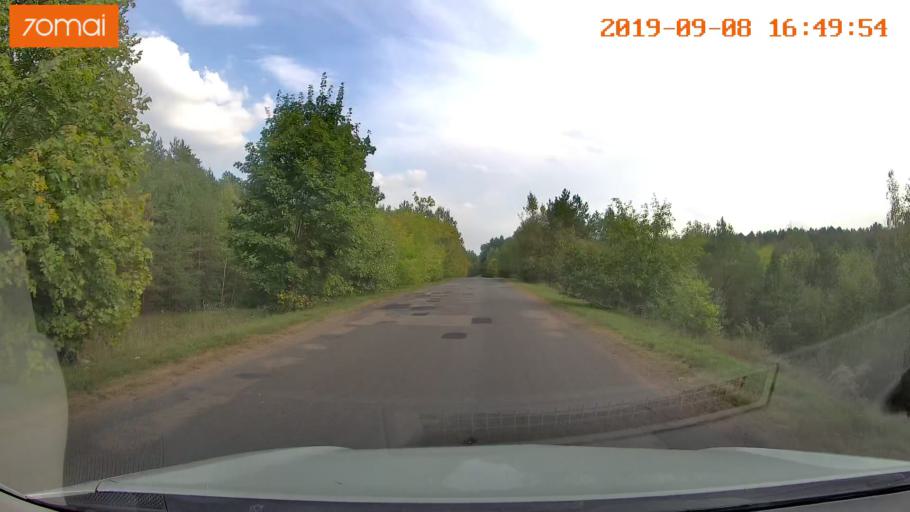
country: BY
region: Grodnenskaya
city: Hrodna
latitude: 53.8059
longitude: 23.8810
